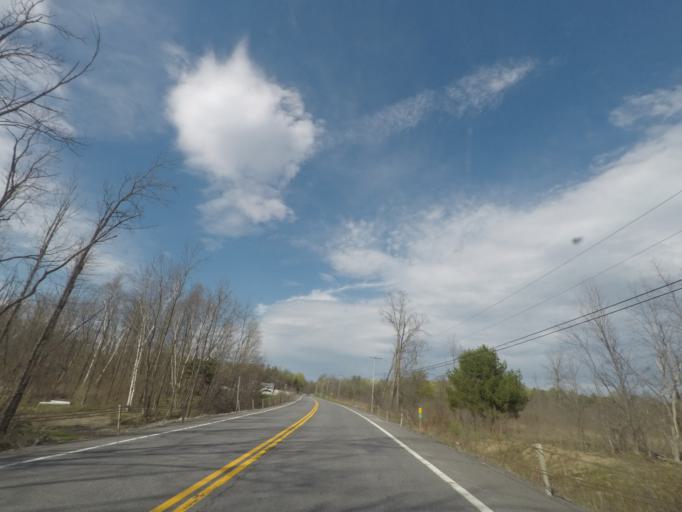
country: US
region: New York
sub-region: Albany County
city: Voorheesville
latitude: 42.5507
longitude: -73.9363
